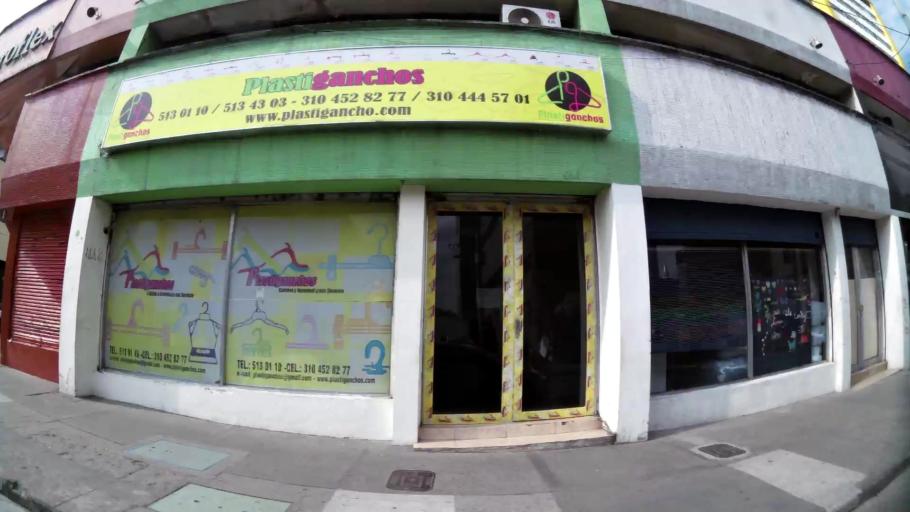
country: CO
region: Antioquia
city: Medellin
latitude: 6.2524
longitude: -75.5737
